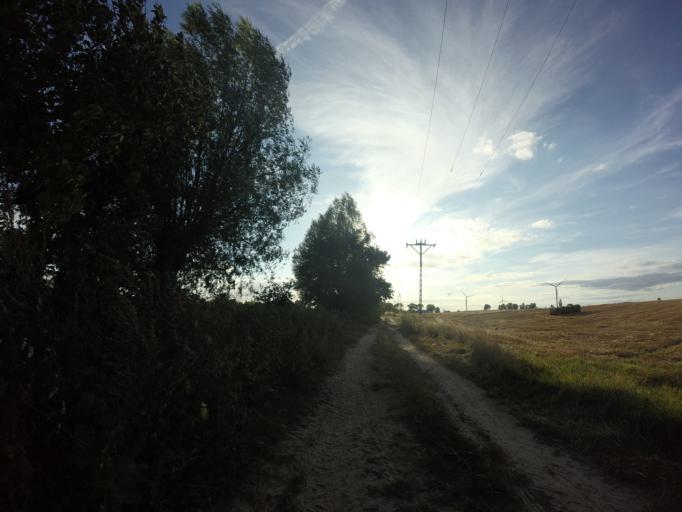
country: PL
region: West Pomeranian Voivodeship
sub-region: Powiat choszczenski
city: Krzecin
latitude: 53.1088
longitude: 15.4570
